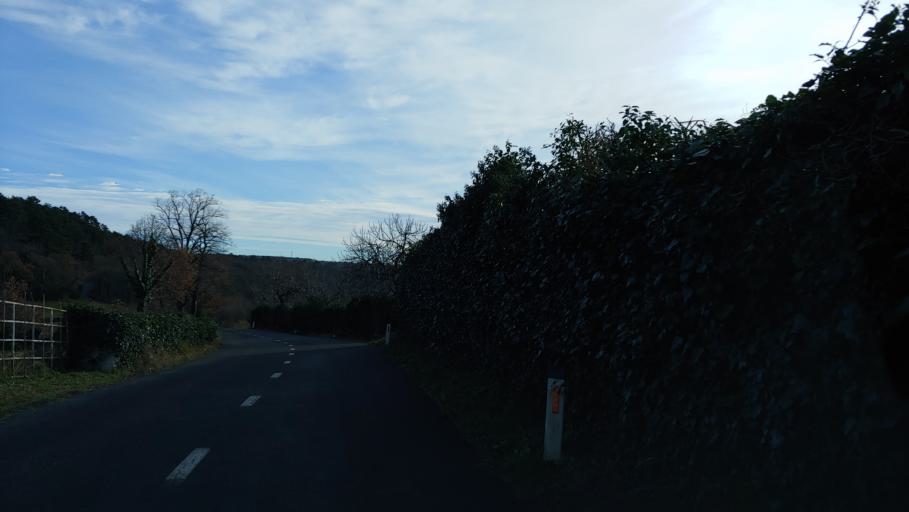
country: SI
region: Komen
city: Komen
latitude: 45.8105
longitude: 13.6955
